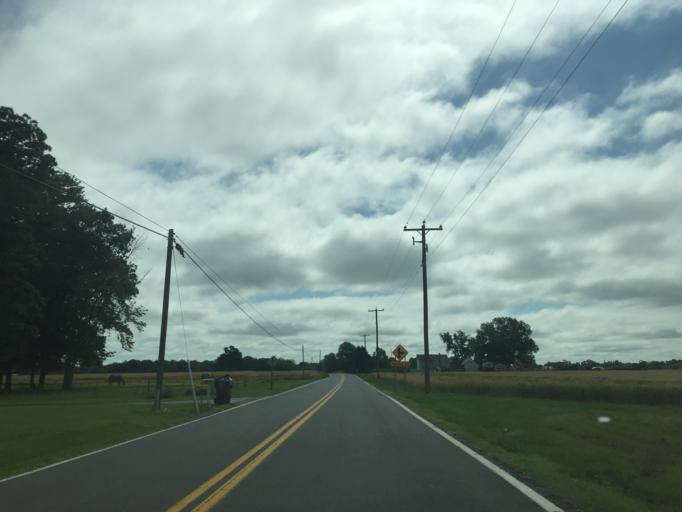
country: US
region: Maryland
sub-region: Caroline County
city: Ridgely
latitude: 38.8851
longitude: -75.9784
